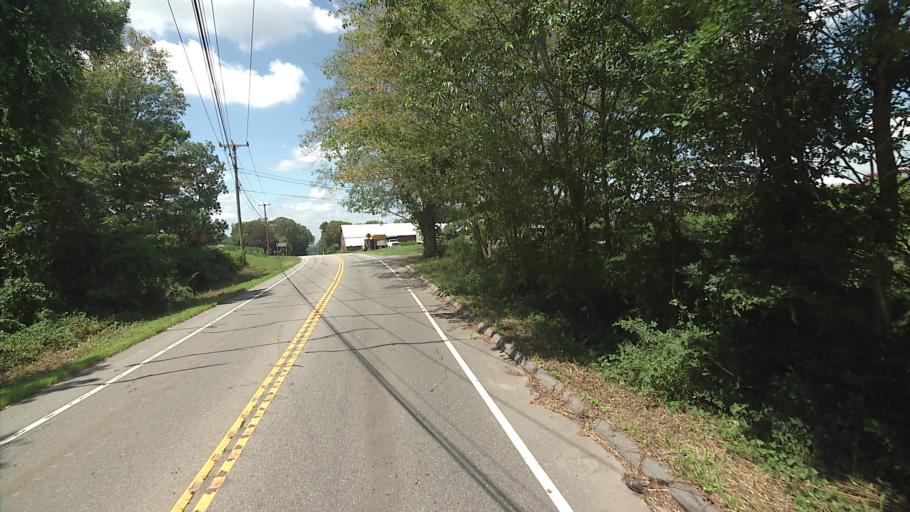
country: US
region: Connecticut
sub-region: New London County
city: Baltic
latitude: 41.6988
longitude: -72.0665
